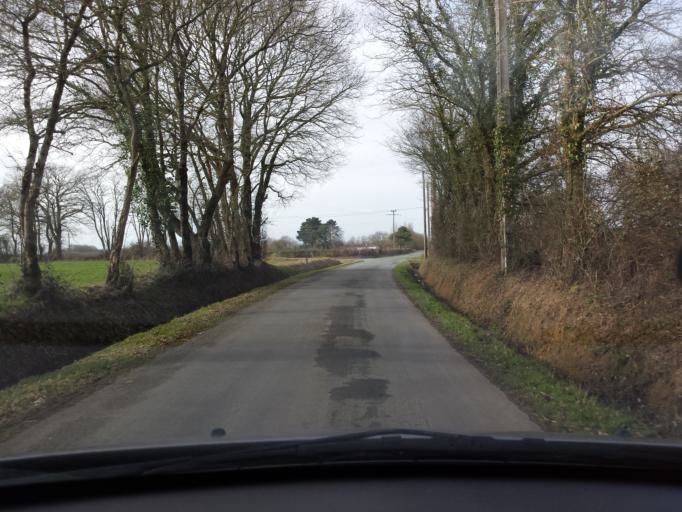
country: FR
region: Pays de la Loire
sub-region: Departement de la Vendee
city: Les Essarts
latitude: 46.7561
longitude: -1.2533
